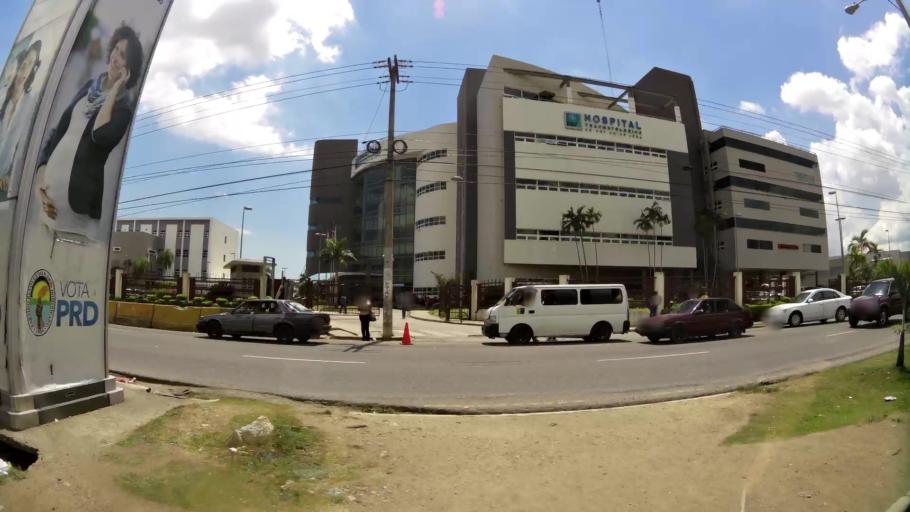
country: DO
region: Nacional
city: Ensanche Luperon
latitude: 18.5481
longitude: -69.8836
